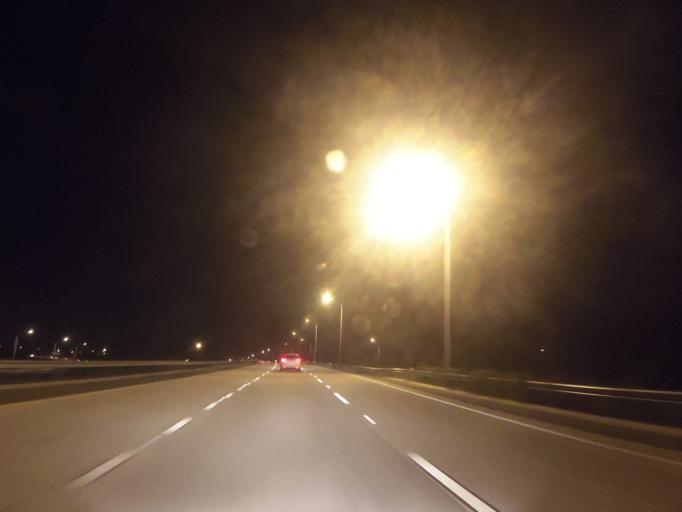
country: US
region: Florida
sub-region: Saint Johns County
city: Fruit Cove
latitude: 30.1089
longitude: -81.5149
